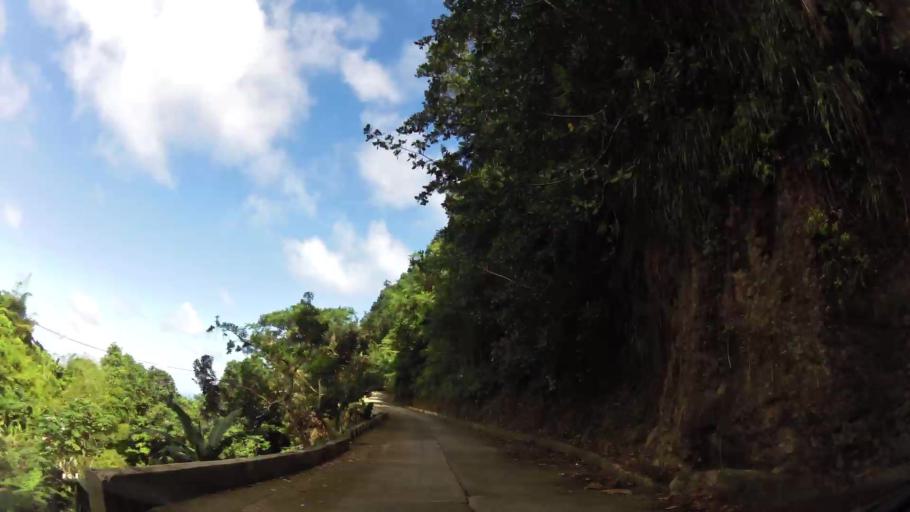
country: DM
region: Saint John
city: Portsmouth
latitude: 15.6252
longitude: -61.4256
